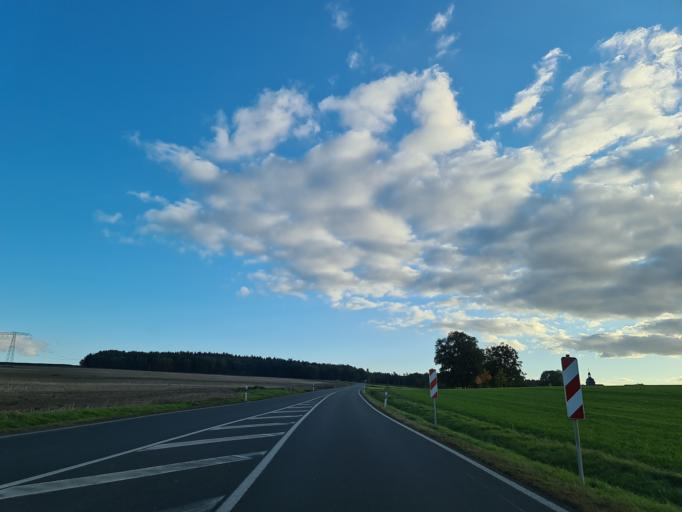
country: DE
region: Thuringia
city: Teichwitz
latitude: 50.7622
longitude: 12.0895
